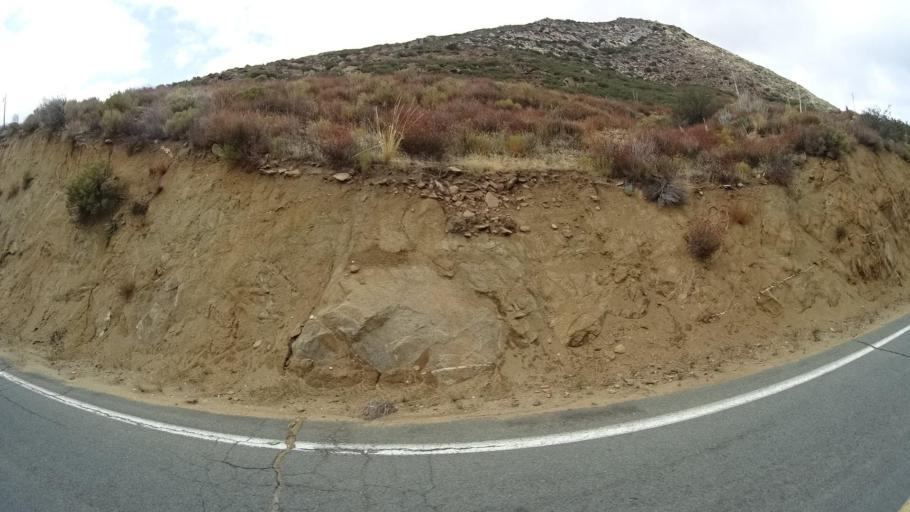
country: US
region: California
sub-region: San Diego County
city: Pine Valley
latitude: 32.7673
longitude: -116.4512
